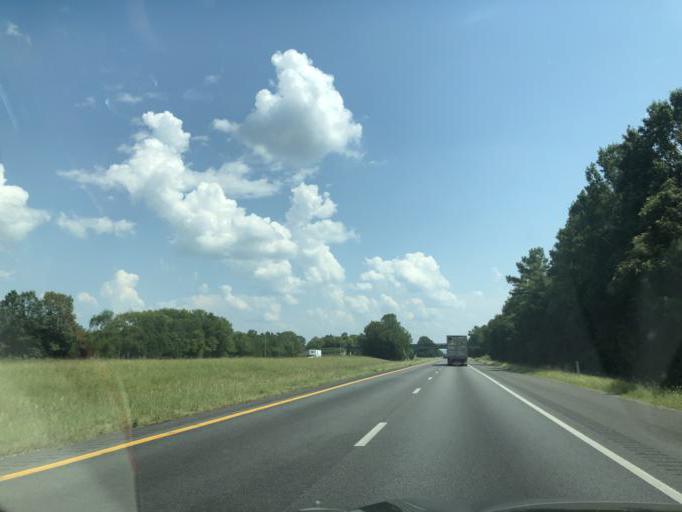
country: US
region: Tennessee
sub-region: Rutherford County
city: Plainview
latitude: 35.7660
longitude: -86.3578
